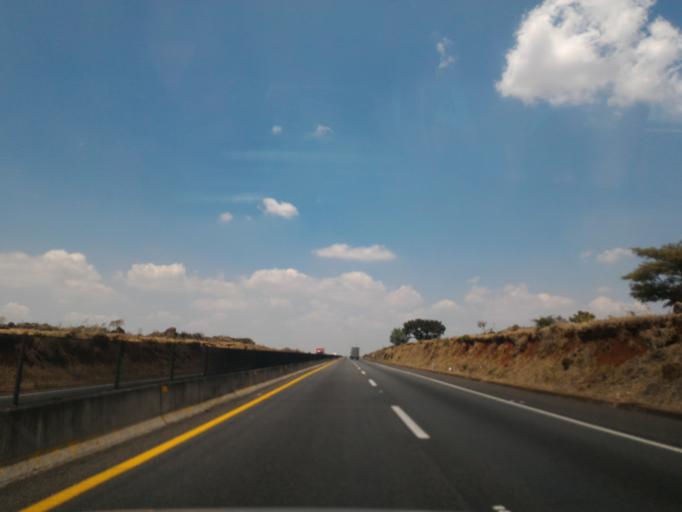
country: MX
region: Jalisco
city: Tepatitlan de Morelos
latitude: 20.8559
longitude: -102.7698
